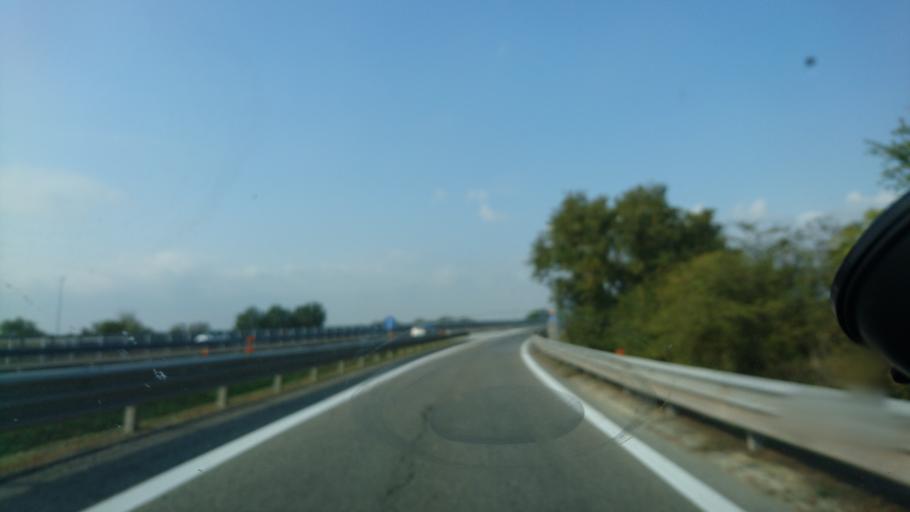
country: IT
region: Piedmont
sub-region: Provincia di Alessandria
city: Castellazzo Bormida
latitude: 44.8743
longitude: 8.5727
